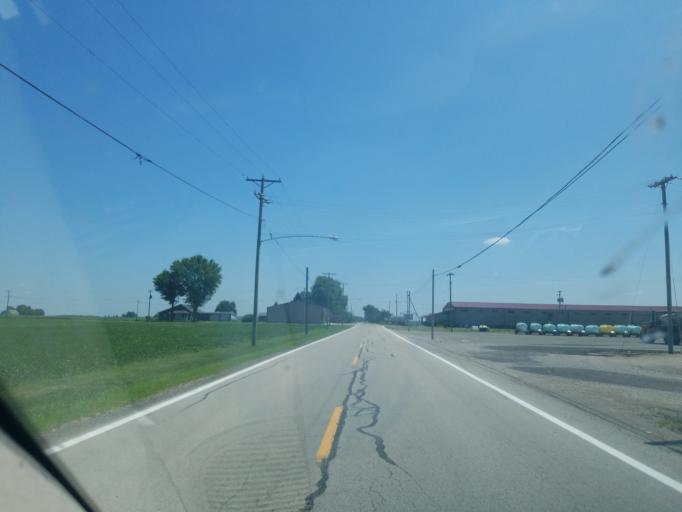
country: US
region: Ohio
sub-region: Allen County
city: Spencerville
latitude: 40.7426
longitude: -84.4772
